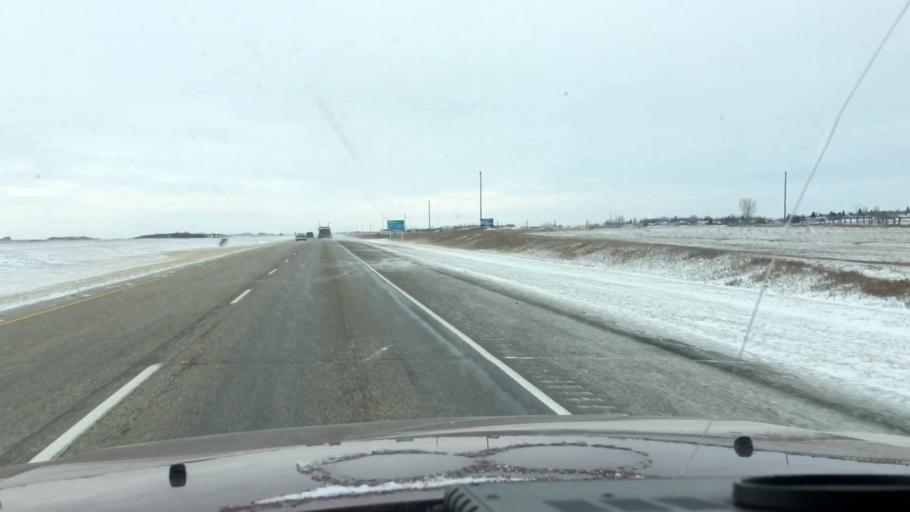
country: CA
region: Saskatchewan
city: Saskatoon
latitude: 51.6428
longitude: -106.4358
